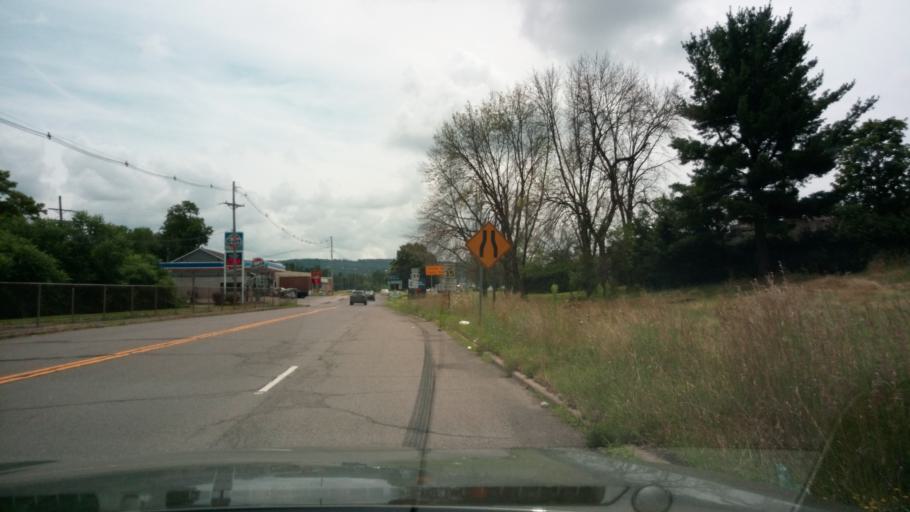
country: US
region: New York
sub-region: Tioga County
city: Waverly
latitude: 41.9987
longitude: -76.5238
